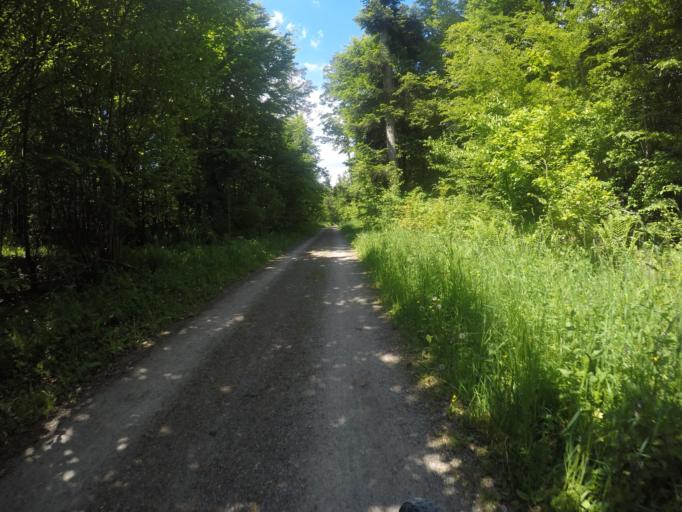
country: DE
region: Baden-Wuerttemberg
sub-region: Regierungsbezirk Stuttgart
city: Unterjettingen
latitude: 48.5849
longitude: 8.8092
